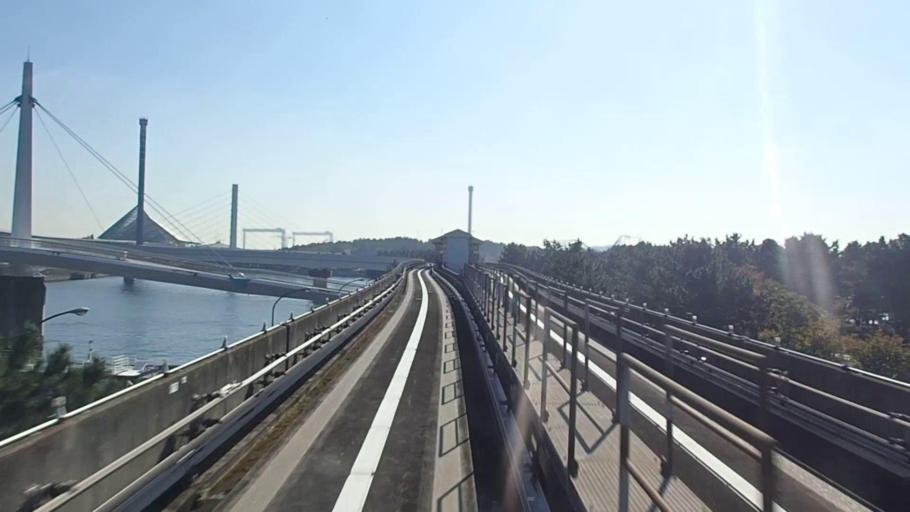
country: JP
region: Kanagawa
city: Yokosuka
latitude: 35.3418
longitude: 139.6401
